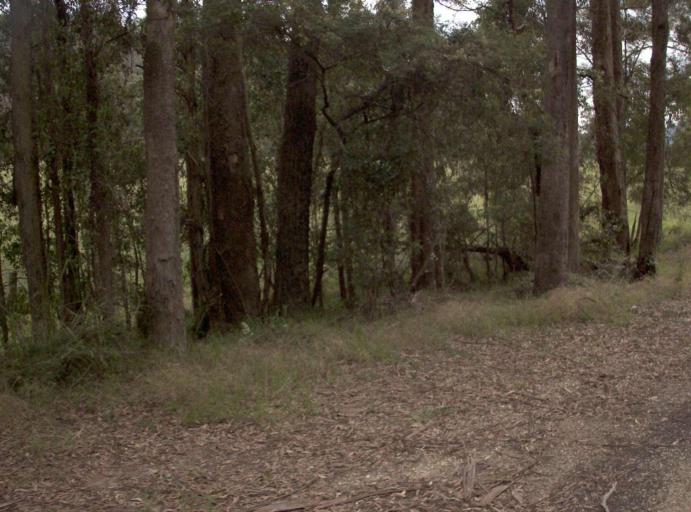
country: AU
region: New South Wales
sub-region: Bombala
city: Bombala
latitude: -37.4594
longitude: 149.1882
